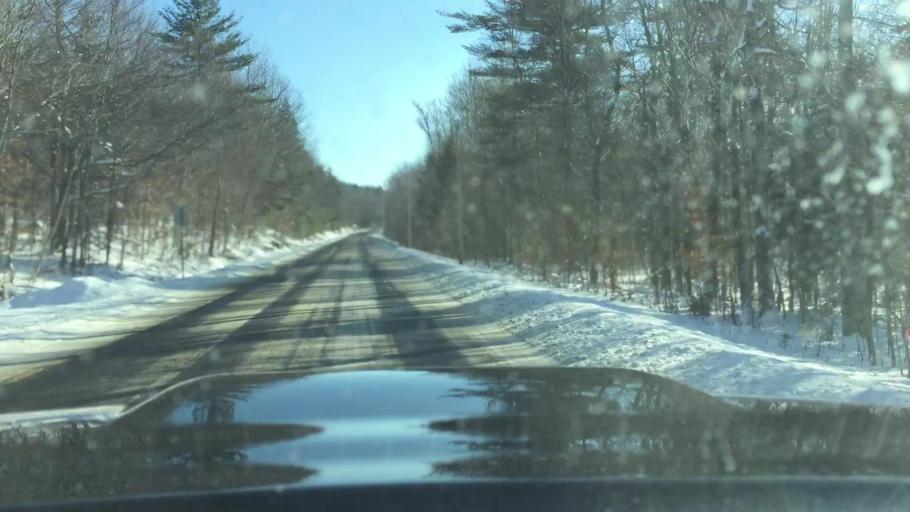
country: US
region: Massachusetts
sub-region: Berkshire County
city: Hinsdale
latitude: 42.4577
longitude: -72.9845
